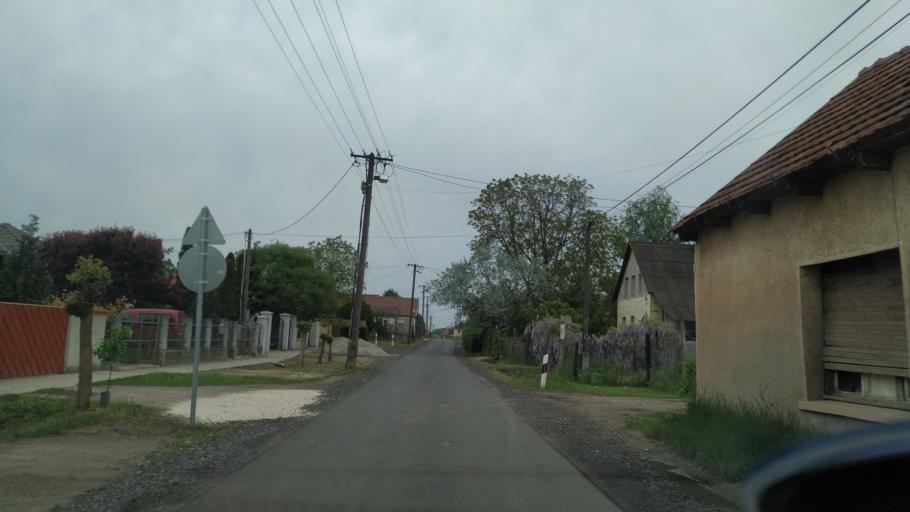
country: HU
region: Pest
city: Nagykata
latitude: 47.4224
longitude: 19.7266
